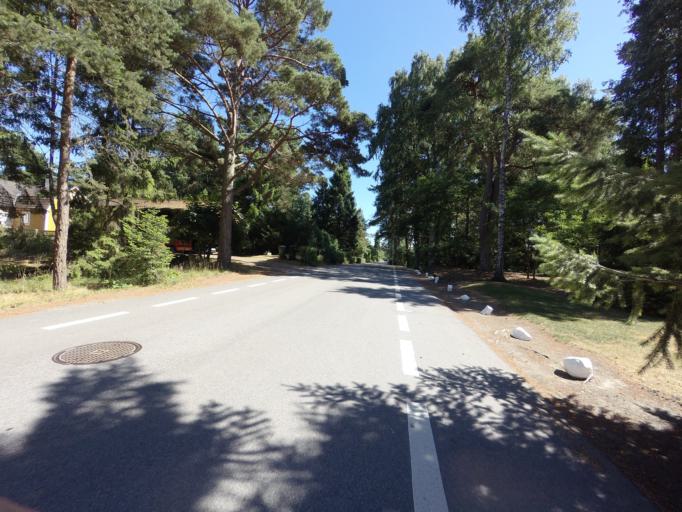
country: SE
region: Skane
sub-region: Vellinge Kommun
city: Hollviken
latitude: 55.4118
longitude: 12.9458
